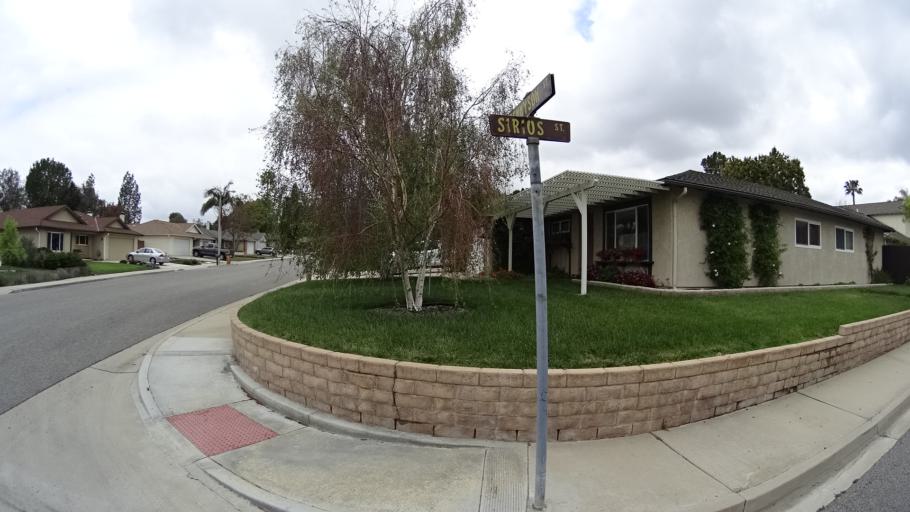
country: US
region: California
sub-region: Ventura County
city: Casa Conejo
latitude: 34.2151
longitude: -118.8872
